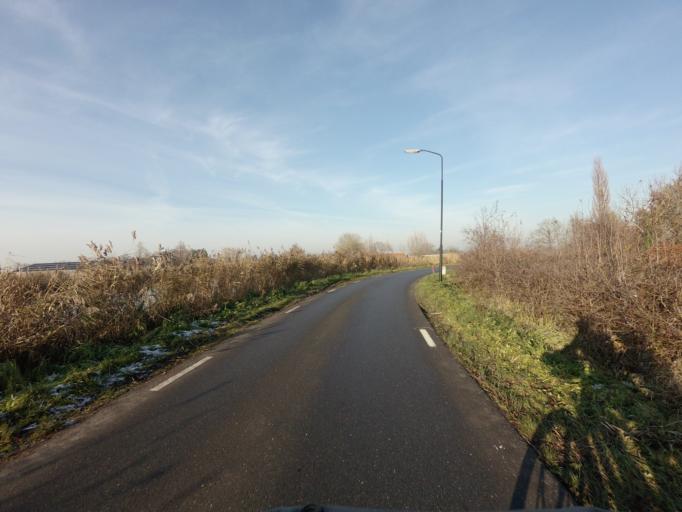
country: NL
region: Utrecht
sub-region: Gemeente De Ronde Venen
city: Mijdrecht
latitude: 52.1901
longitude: 4.8288
